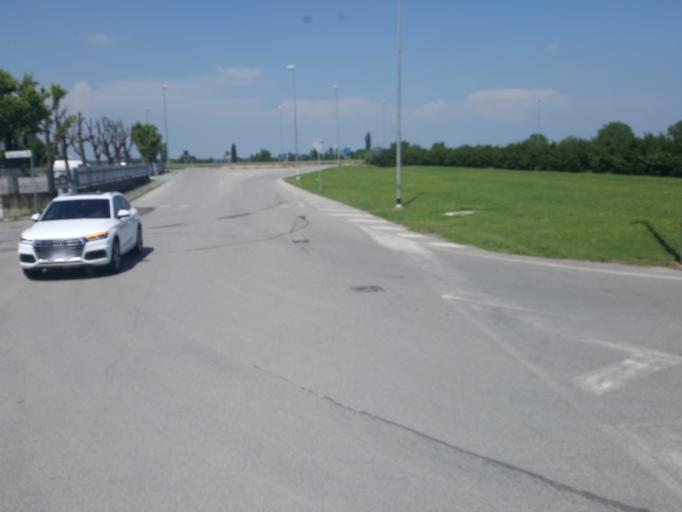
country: IT
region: Lombardy
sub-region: Provincia di Cremona
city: Calvatone
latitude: 45.1158
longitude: 10.4535
